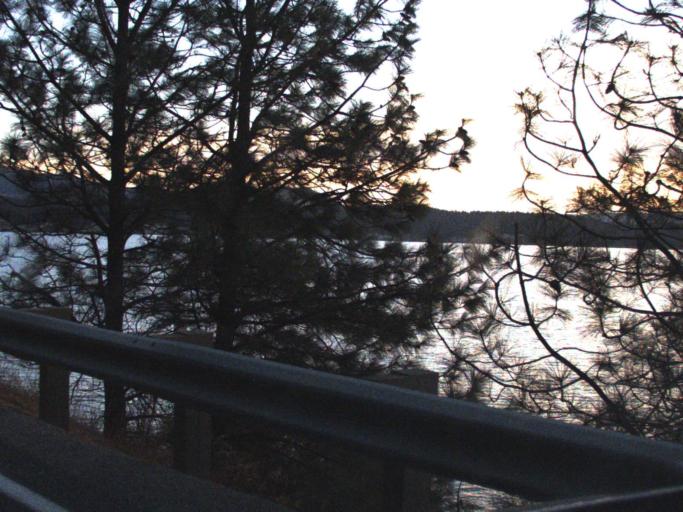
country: US
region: Washington
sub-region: Stevens County
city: Kettle Falls
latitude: 48.6499
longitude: -118.0836
